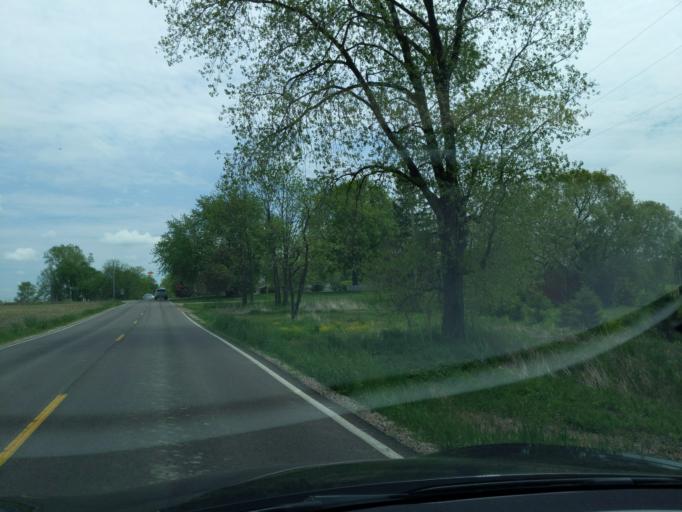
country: US
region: Michigan
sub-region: Ingham County
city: Stockbridge
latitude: 42.4684
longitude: -84.1617
